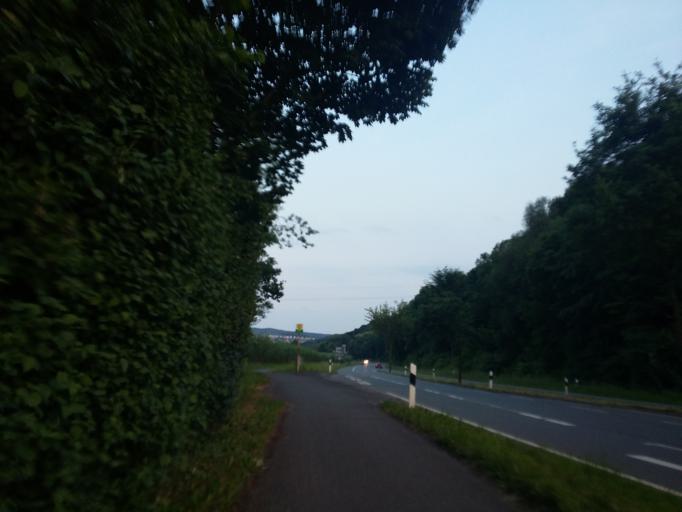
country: DE
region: North Rhine-Westphalia
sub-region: Regierungsbezirk Detmold
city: Vlotho
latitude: 52.1945
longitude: 8.8524
